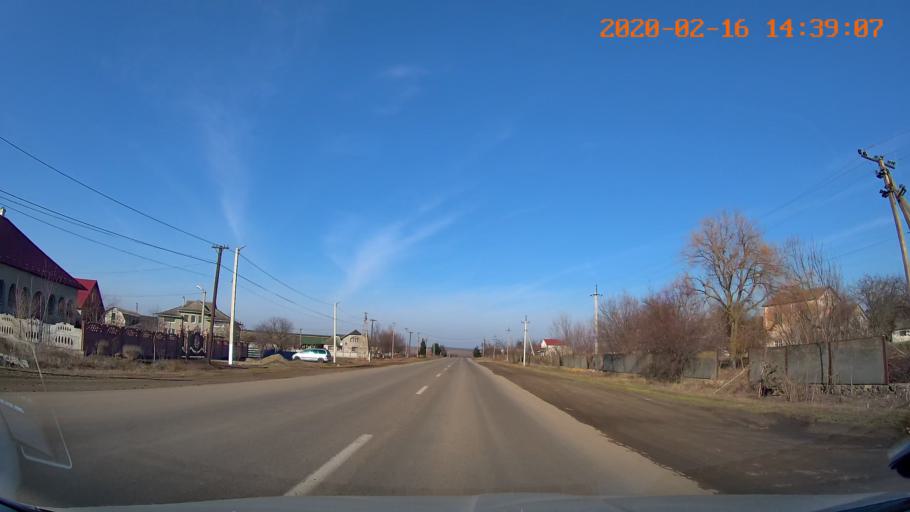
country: RO
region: Botosani
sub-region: Comuna Darabani
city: Bajura
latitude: 48.2387
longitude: 26.5473
